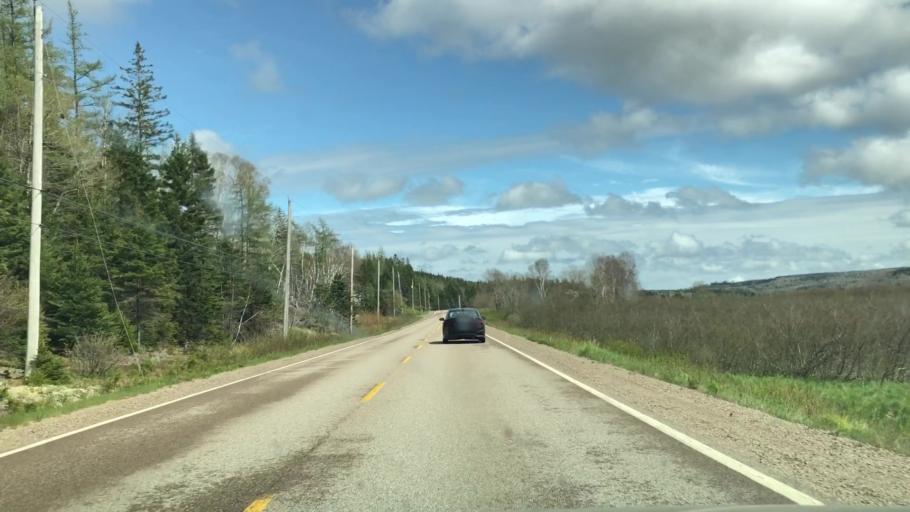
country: CA
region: Nova Scotia
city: Antigonish
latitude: 45.1931
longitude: -61.9954
